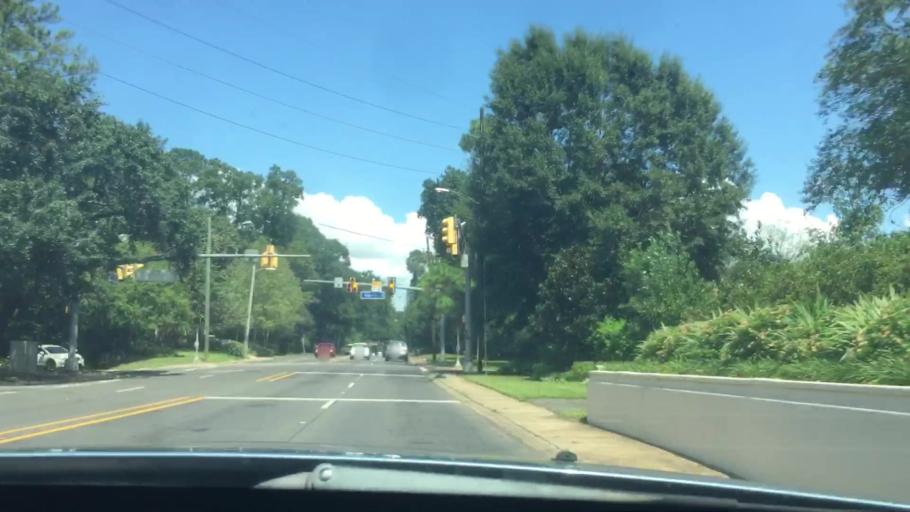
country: US
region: Louisiana
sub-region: East Baton Rouge Parish
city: Baton Rouge
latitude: 30.4134
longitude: -91.1587
